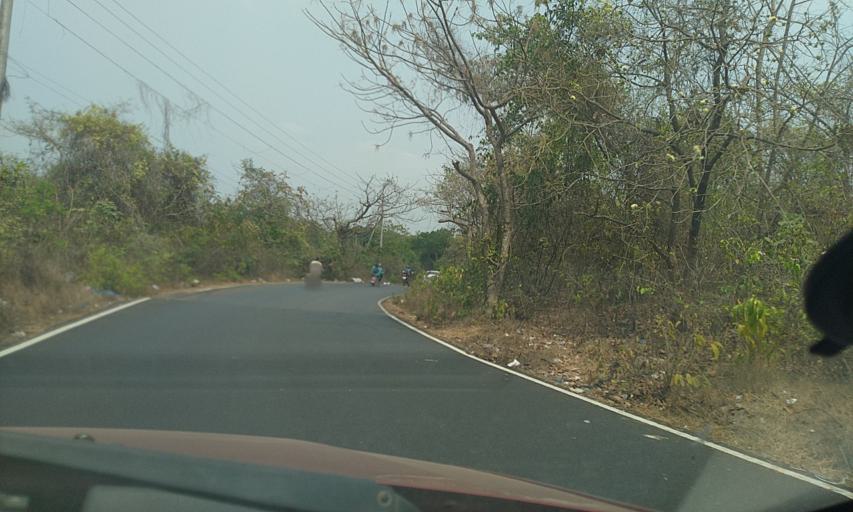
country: IN
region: Goa
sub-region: North Goa
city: Mapuca
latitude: 15.6108
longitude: 73.7958
